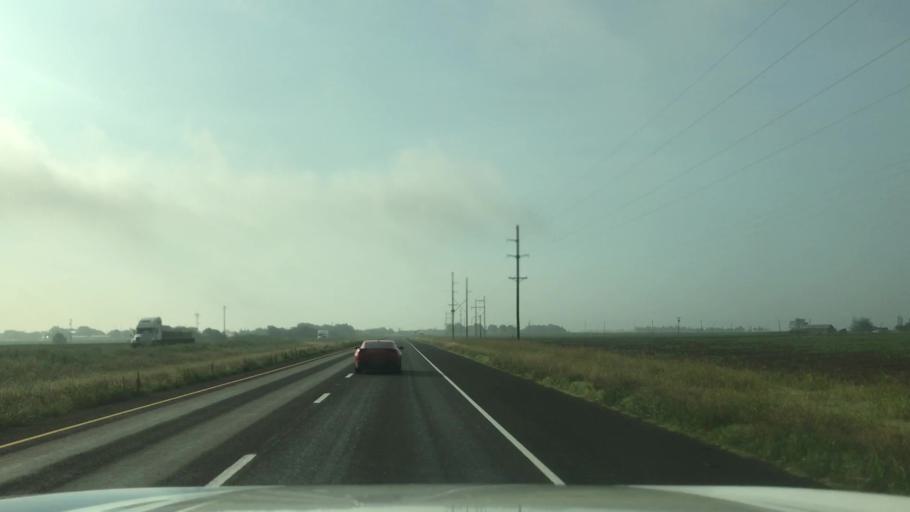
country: US
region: Texas
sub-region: Lubbock County
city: Slaton
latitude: 33.3644
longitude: -101.5630
